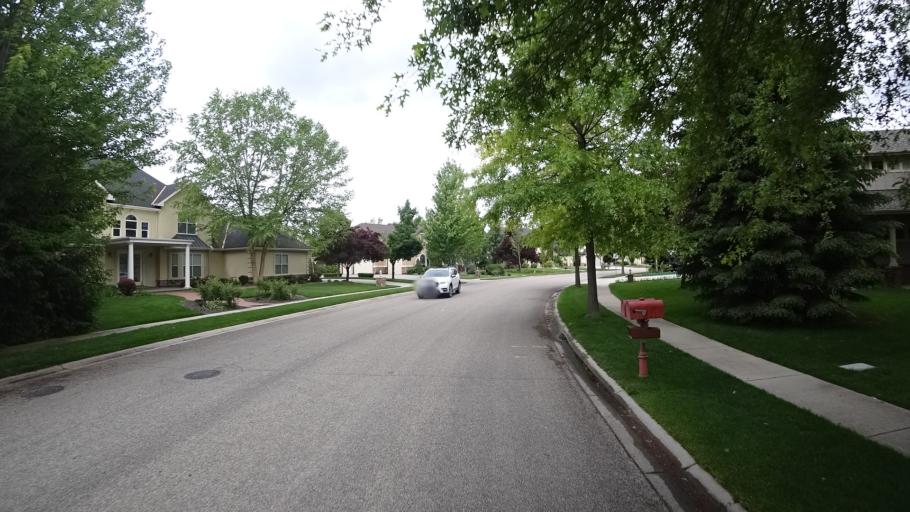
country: US
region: Idaho
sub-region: Ada County
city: Eagle
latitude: 43.6805
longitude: -116.3597
